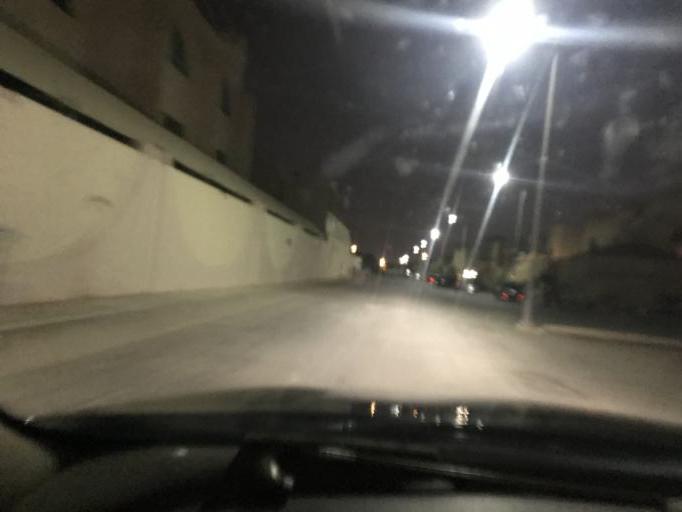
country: SA
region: Ar Riyad
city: Riyadh
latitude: 24.7995
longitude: 46.7091
